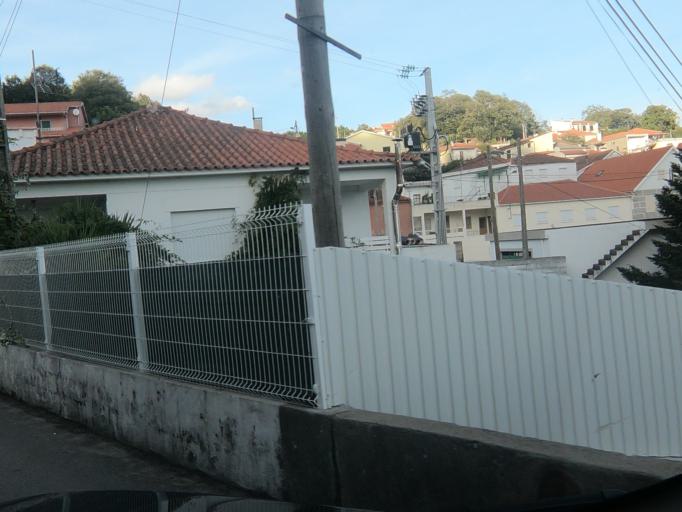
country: PT
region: Vila Real
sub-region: Santa Marta de Penaguiao
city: Santa Marta de Penaguiao
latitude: 41.2299
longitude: -7.8163
